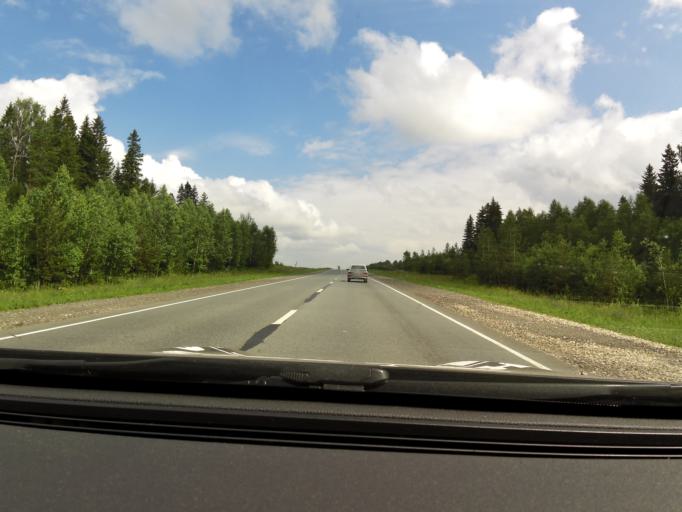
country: RU
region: Perm
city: Suksun
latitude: 57.1603
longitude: 57.2238
